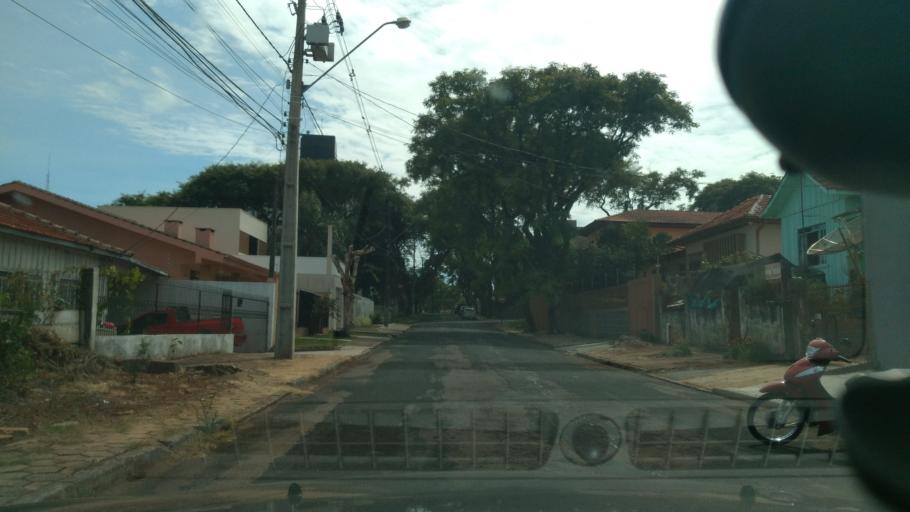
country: BR
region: Parana
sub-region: Guarapuava
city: Guarapuava
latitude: -25.3867
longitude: -51.4665
